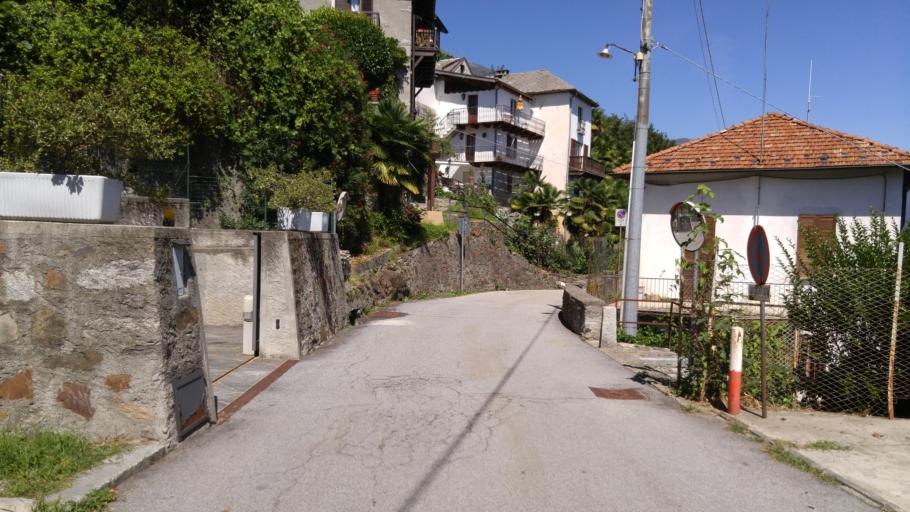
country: IT
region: Piedmont
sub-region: Provincia Verbano-Cusio-Ossola
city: Cannobio
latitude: 46.0711
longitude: 8.6868
